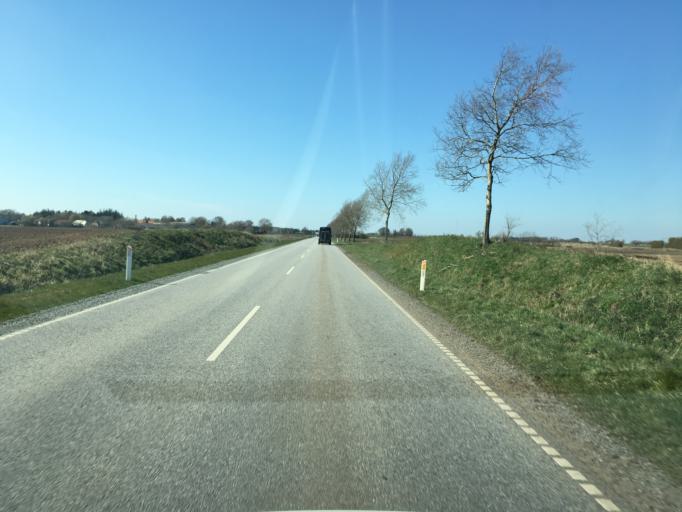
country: DK
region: South Denmark
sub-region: Aabenraa Kommune
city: Tinglev
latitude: 54.9638
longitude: 9.3230
